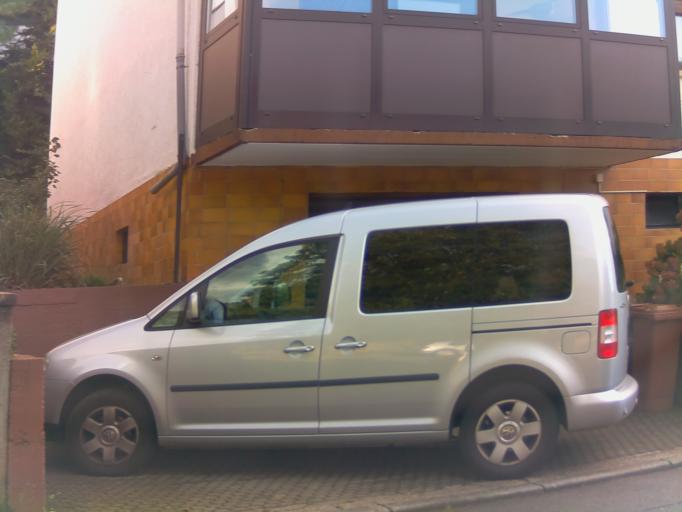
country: DE
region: Baden-Wuerttemberg
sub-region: Karlsruhe Region
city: Weinheim
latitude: 49.5268
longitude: 8.6734
